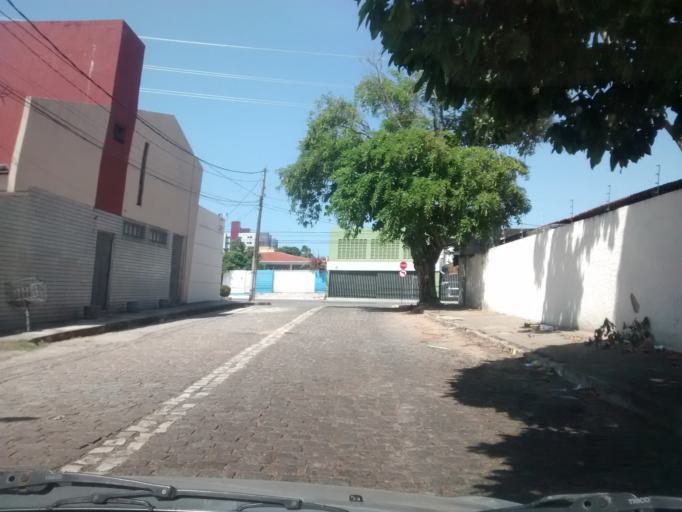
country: BR
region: Rio Grande do Norte
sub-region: Natal
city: Natal
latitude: -5.8180
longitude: -35.2172
